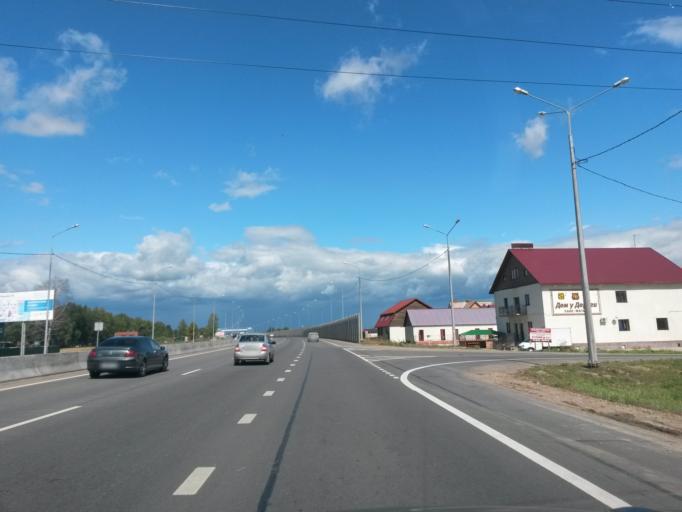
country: RU
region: Jaroslavl
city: Yaroslavl
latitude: 57.7101
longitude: 39.9033
